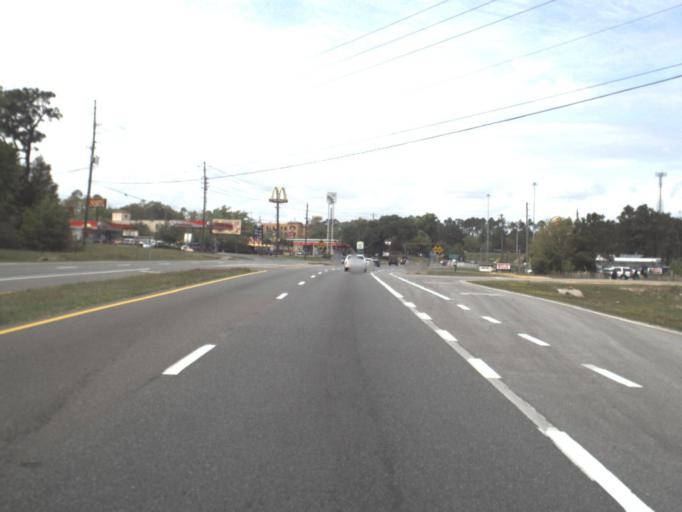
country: US
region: Florida
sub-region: Escambia County
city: Ensley
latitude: 30.5167
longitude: -87.3119
